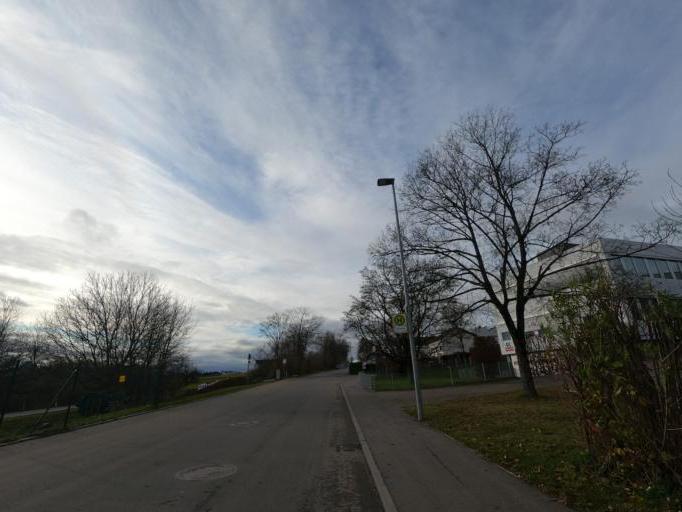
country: DE
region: Baden-Wuerttemberg
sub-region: Regierungsbezirk Stuttgart
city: Albershausen
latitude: 48.6869
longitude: 9.5530
